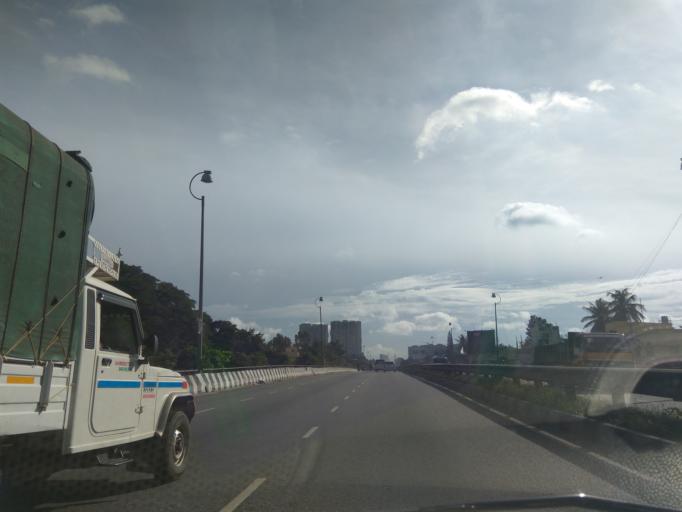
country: IN
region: Karnataka
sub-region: Bangalore Rural
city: Hoskote
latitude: 13.0355
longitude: 77.7355
